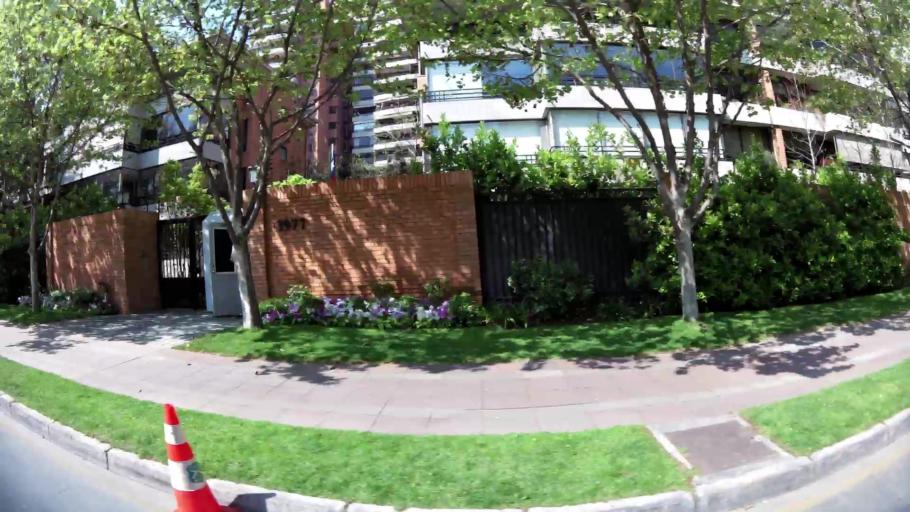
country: CL
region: Santiago Metropolitan
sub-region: Provincia de Santiago
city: Villa Presidente Frei, Nunoa, Santiago, Chile
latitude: -33.3970
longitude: -70.6004
